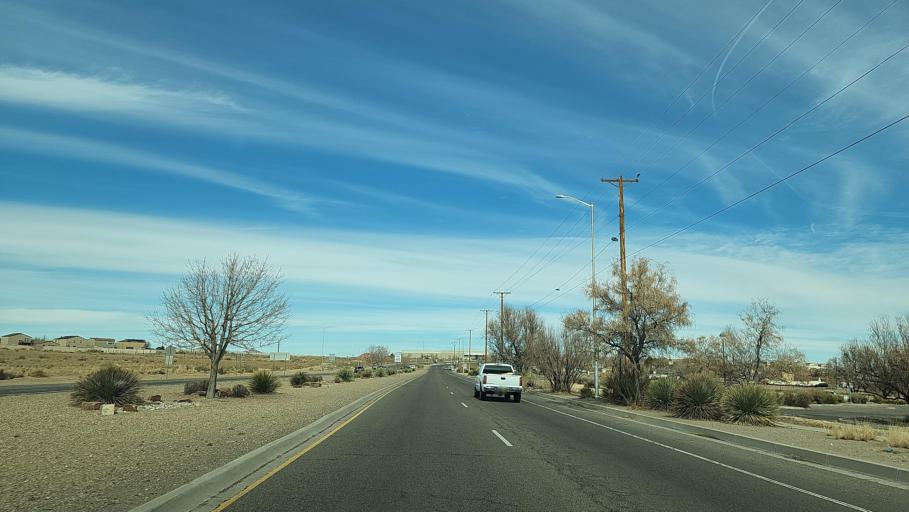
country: US
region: New Mexico
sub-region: Bernalillo County
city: Albuquerque
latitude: 35.0707
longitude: -106.7121
